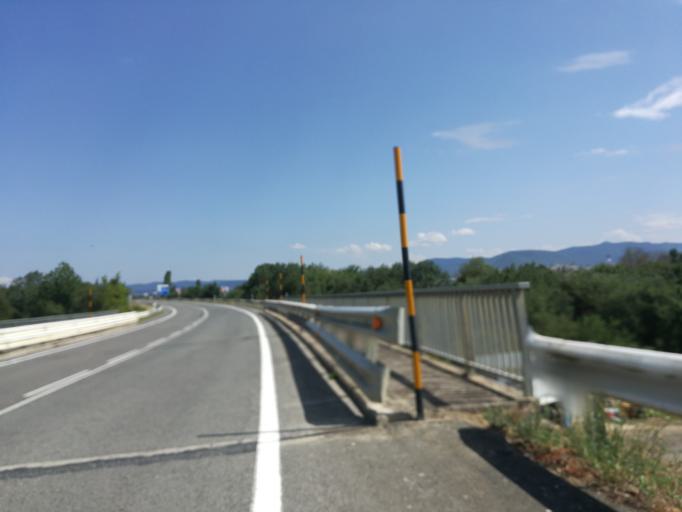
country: ES
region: Basque Country
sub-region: Provincia de Alava
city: Gasteiz / Vitoria
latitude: 42.8637
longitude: -2.7445
